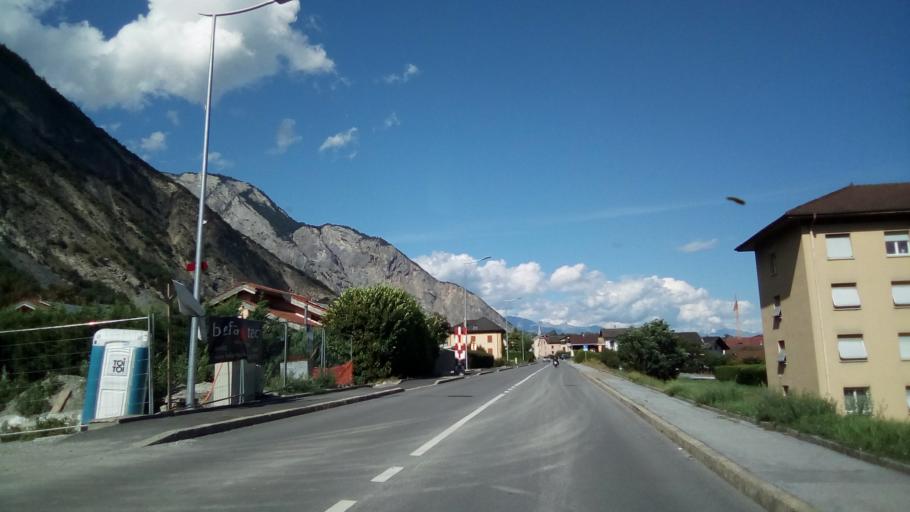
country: CH
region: Valais
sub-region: Martigny District
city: Leytron
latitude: 46.1837
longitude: 7.2045
